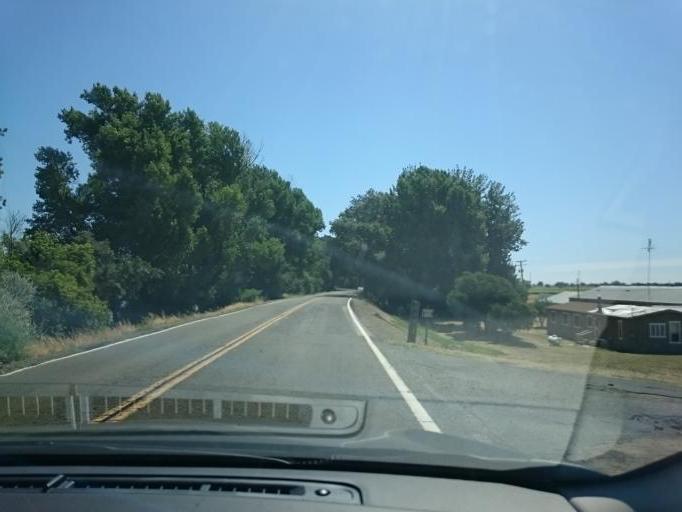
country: US
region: California
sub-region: Sacramento County
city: Parkway
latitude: 38.4731
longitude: -121.5250
